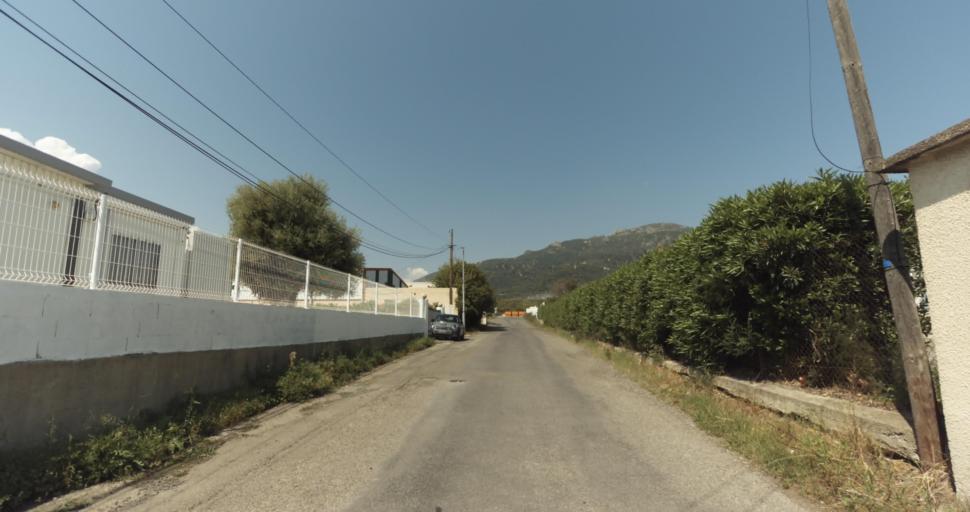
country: FR
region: Corsica
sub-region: Departement de la Haute-Corse
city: Biguglia
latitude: 42.6139
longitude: 9.4364
